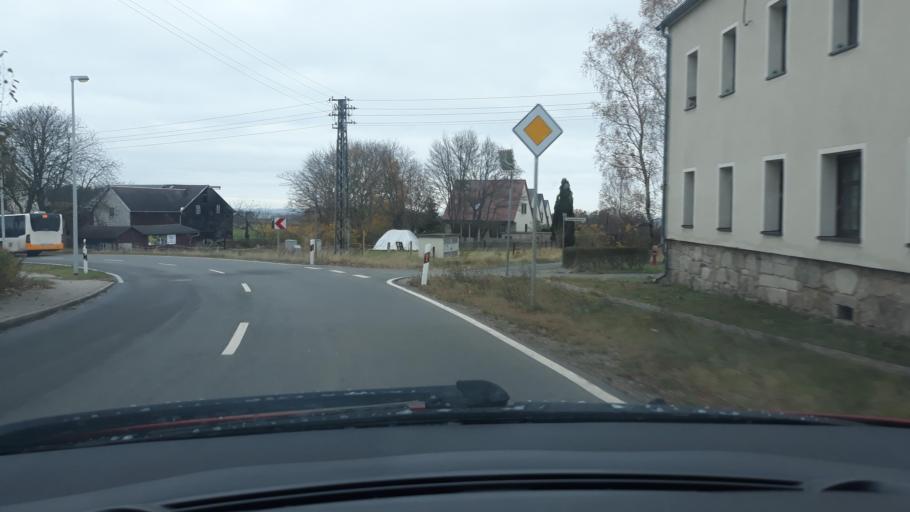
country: DE
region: Saxony
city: Kirchberg
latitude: 50.6294
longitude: 12.5582
